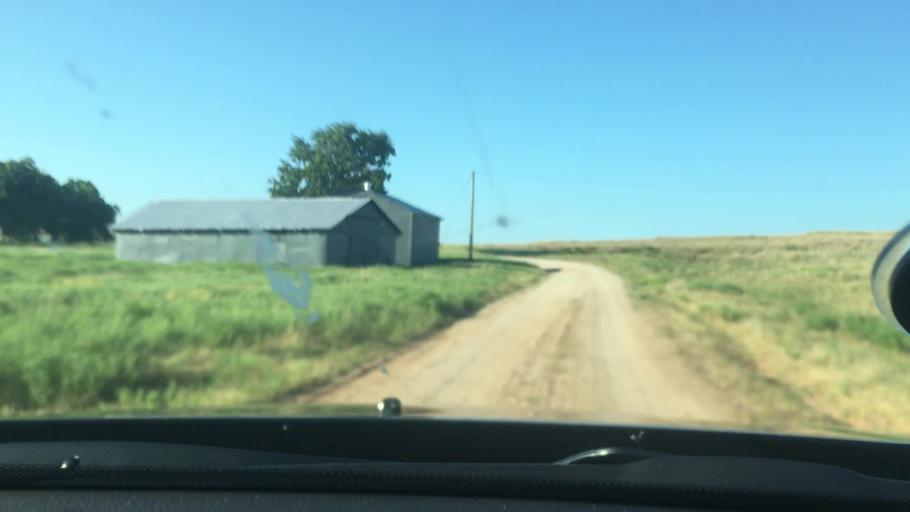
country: US
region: Oklahoma
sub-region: Johnston County
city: Tishomingo
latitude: 34.4189
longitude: -96.7600
